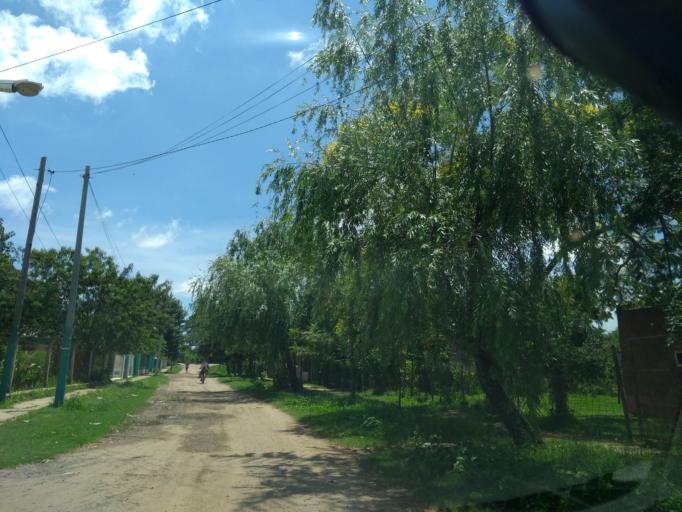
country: AR
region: Chaco
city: Resistencia
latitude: -27.4589
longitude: -58.9622
